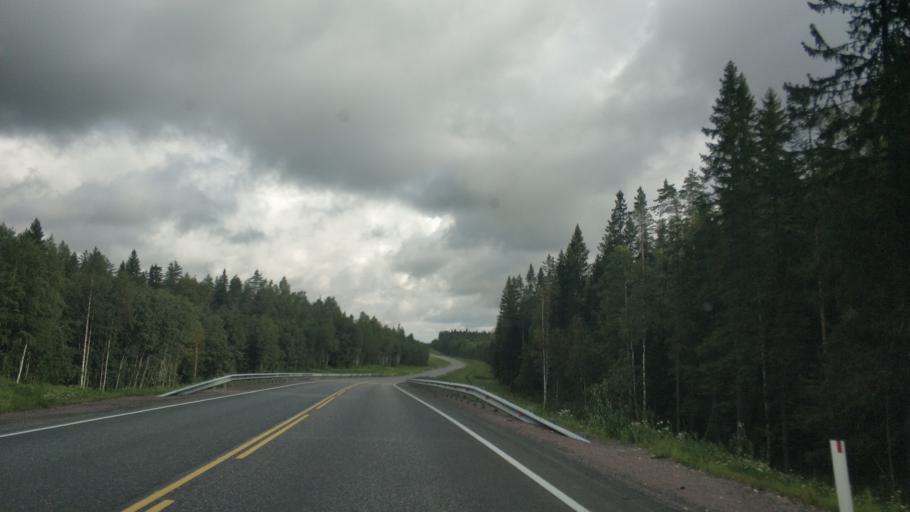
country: RU
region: Republic of Karelia
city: Khelyulya
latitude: 61.8510
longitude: 30.6503
